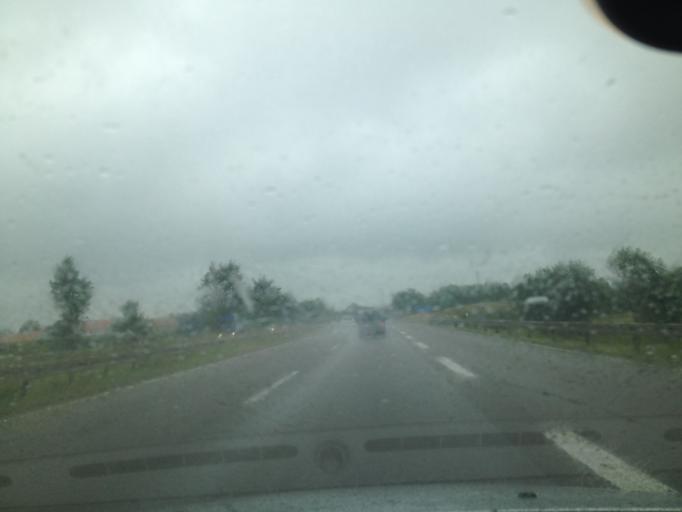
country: DE
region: Hesse
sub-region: Regierungsbezirk Darmstadt
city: Langenselbold
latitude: 50.1779
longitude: 9.0142
